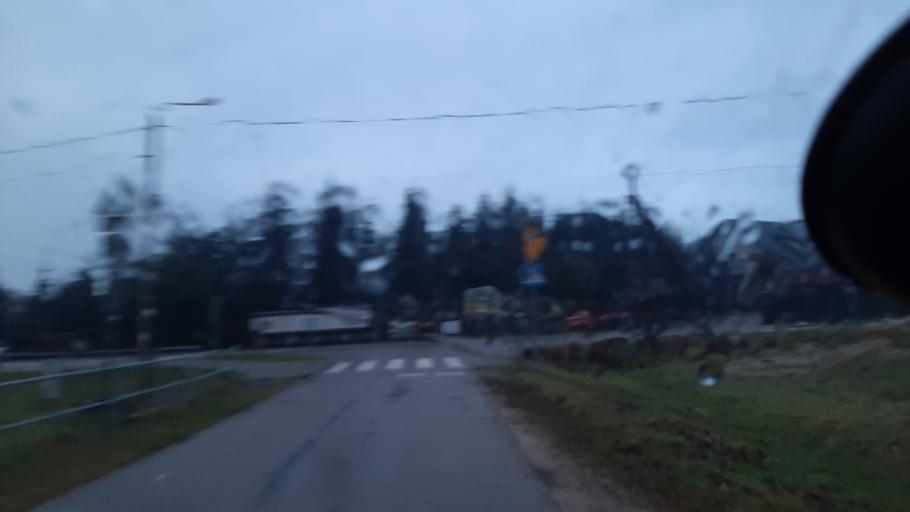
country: PL
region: Lublin Voivodeship
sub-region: Powiat lubartowski
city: Firlej
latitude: 51.5583
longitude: 22.5232
